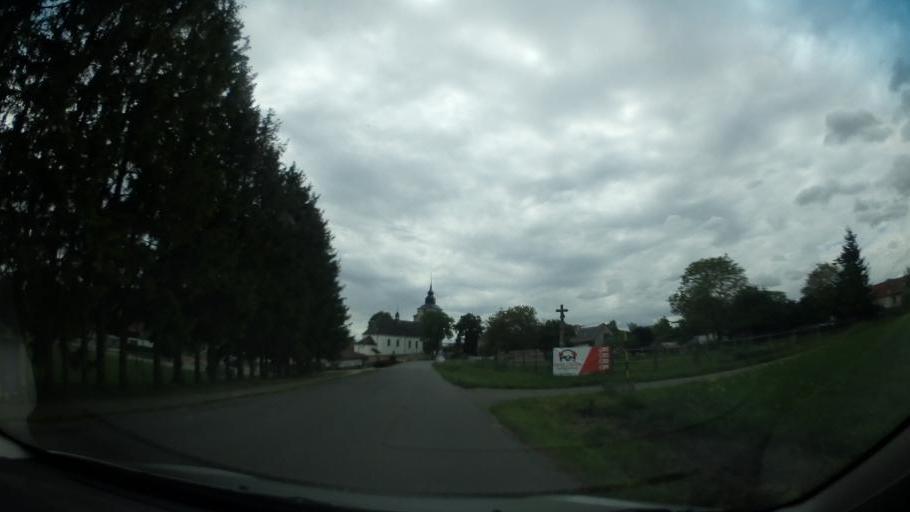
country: CZ
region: Pardubicky
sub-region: Okres Svitavy
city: Moravska Trebova
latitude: 49.7962
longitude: 16.6780
